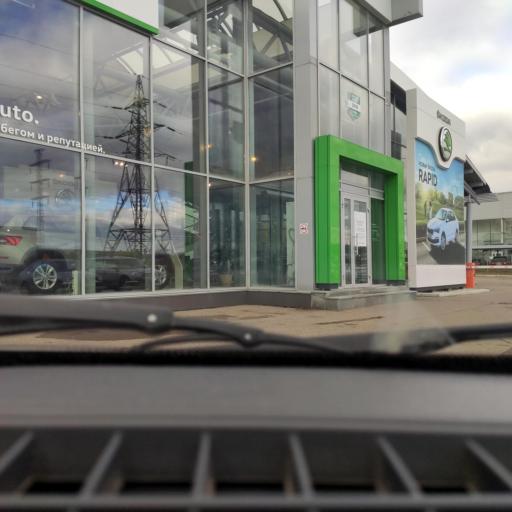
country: RU
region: Bashkortostan
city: Ufa
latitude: 54.7986
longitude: 56.0558
